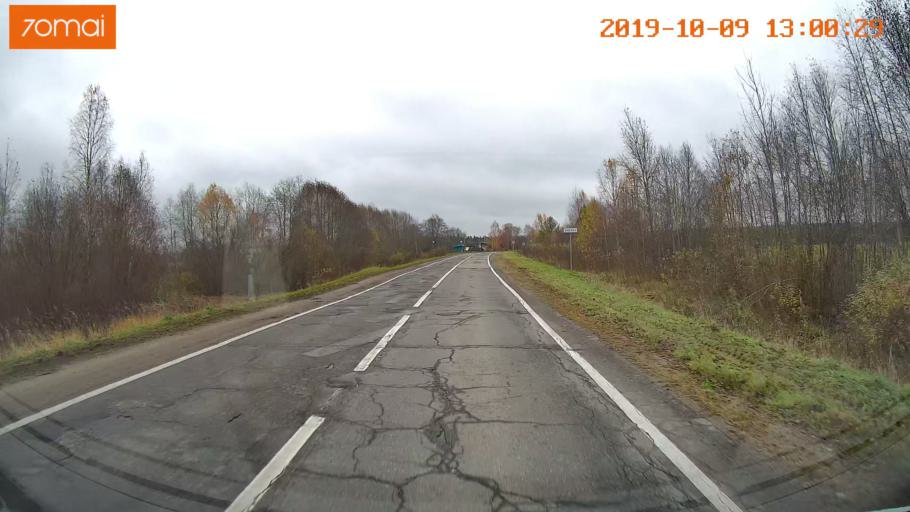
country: RU
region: Jaroslavl
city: Prechistoye
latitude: 58.3769
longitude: 40.4807
